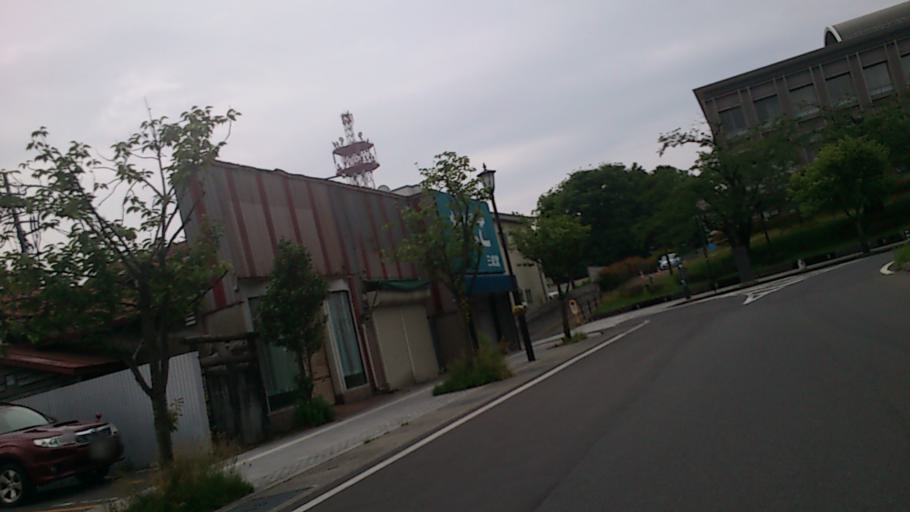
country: JP
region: Aomori
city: Hirosaki
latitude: 40.6037
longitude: 140.4676
